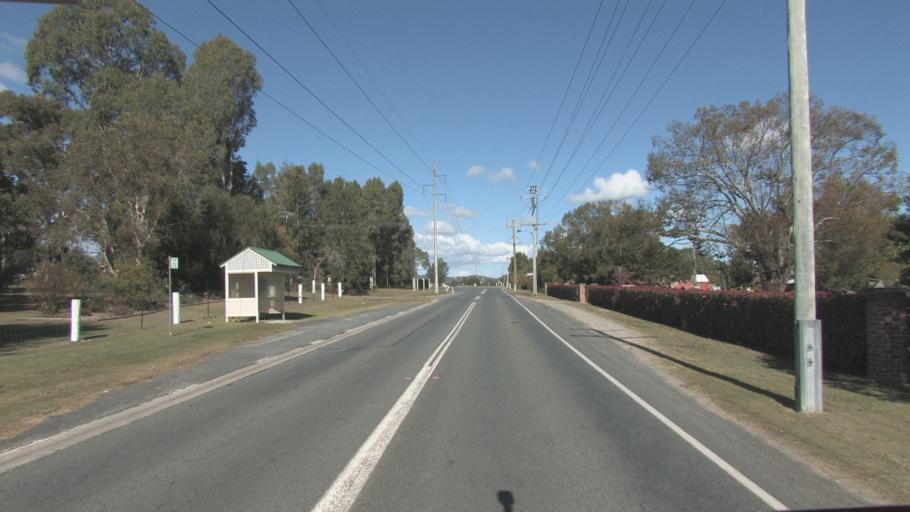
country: AU
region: Queensland
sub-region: Logan
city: Chambers Flat
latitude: -27.7590
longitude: 153.0912
